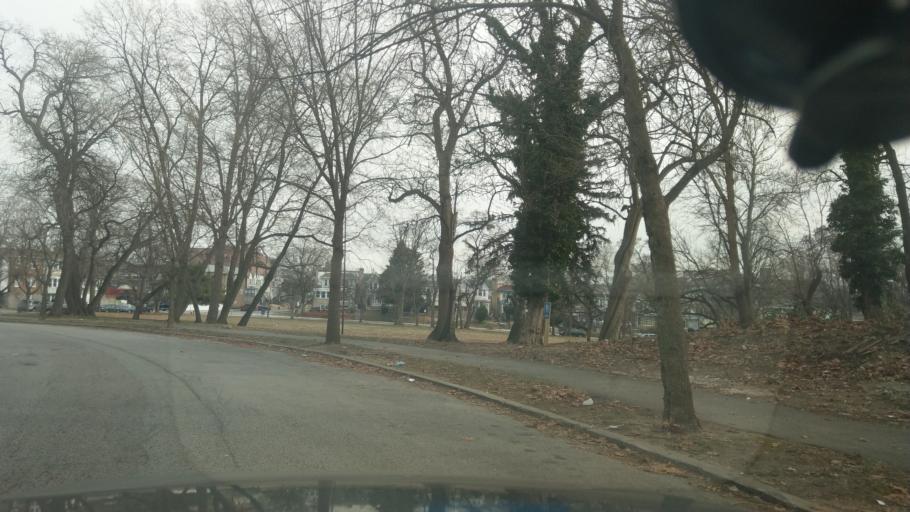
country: US
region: Pennsylvania
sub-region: Montgomery County
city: Wyncote
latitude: 40.0403
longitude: -75.1498
